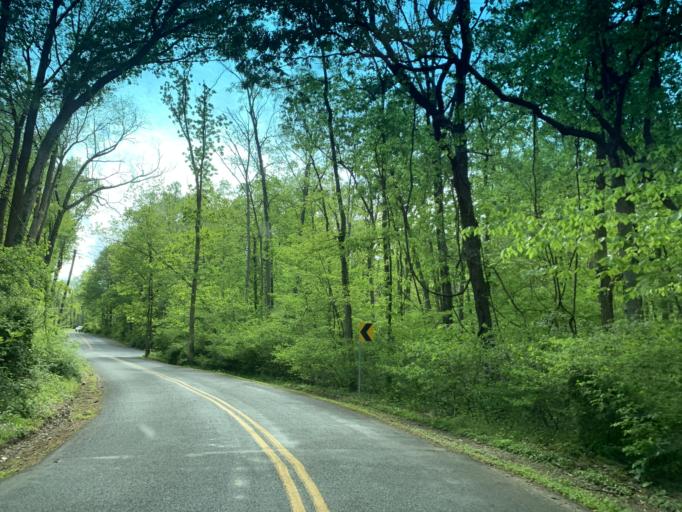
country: US
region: Maryland
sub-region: Harford County
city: South Bel Air
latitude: 39.6405
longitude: -76.2399
